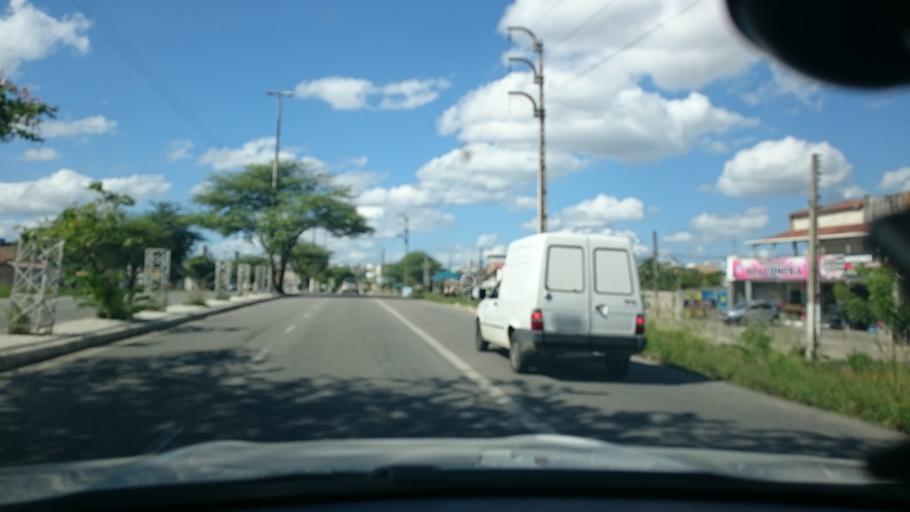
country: BR
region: Paraiba
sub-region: Campina Grande
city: Campina Grande
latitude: -7.2369
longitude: -35.9224
